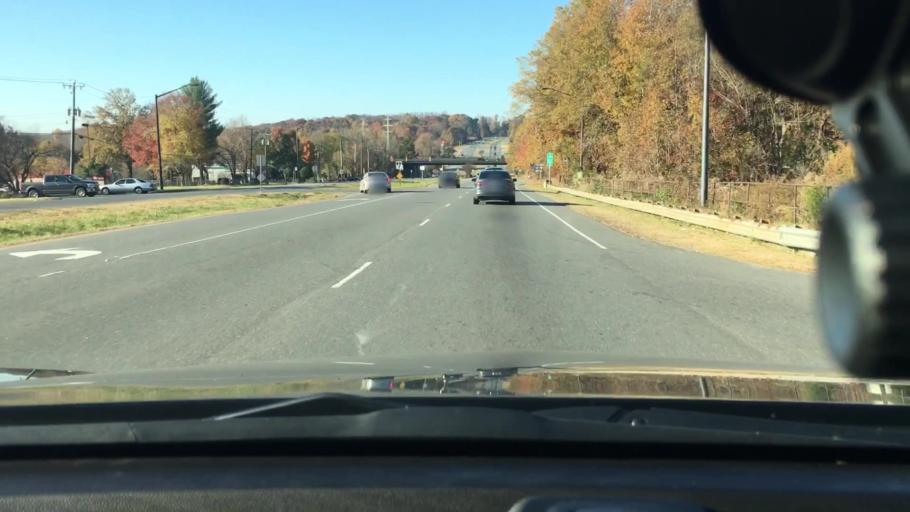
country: US
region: North Carolina
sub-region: Cabarrus County
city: Harrisburg
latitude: 35.2978
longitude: -80.7393
